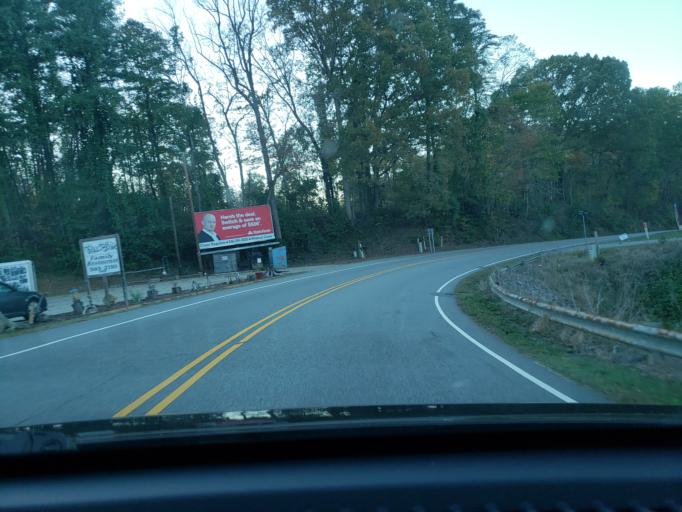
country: US
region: North Carolina
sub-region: Stokes County
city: Danbury
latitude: 36.3999
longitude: -80.2020
